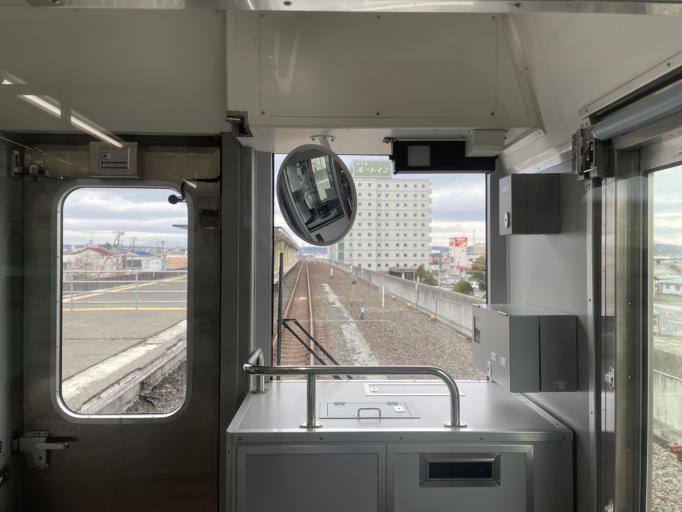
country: JP
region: Aomori
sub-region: Hachinohe Shi
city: Uchimaru
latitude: 40.5163
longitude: 141.4899
